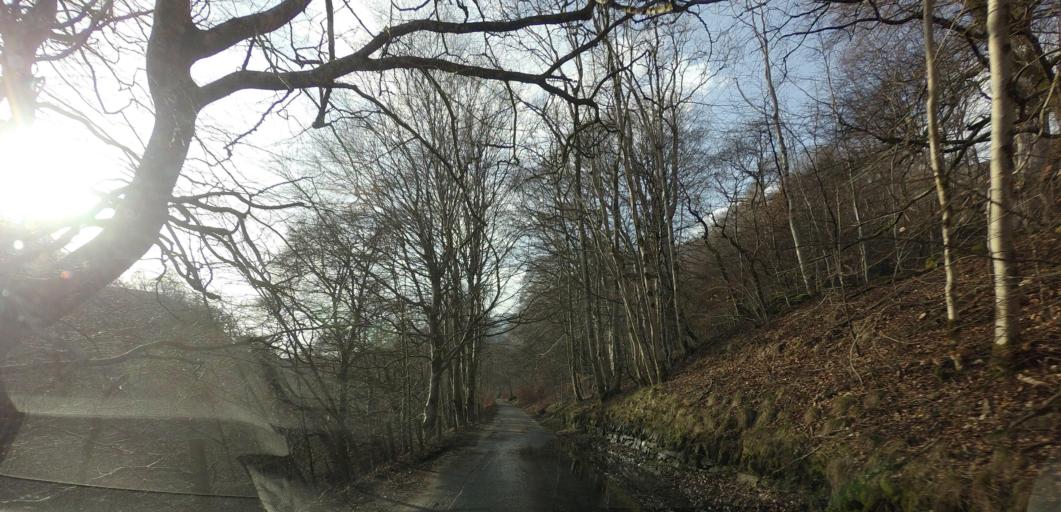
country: GB
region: Scotland
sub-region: Perth and Kinross
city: Aberfeldy
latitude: 56.6029
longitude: -4.0754
